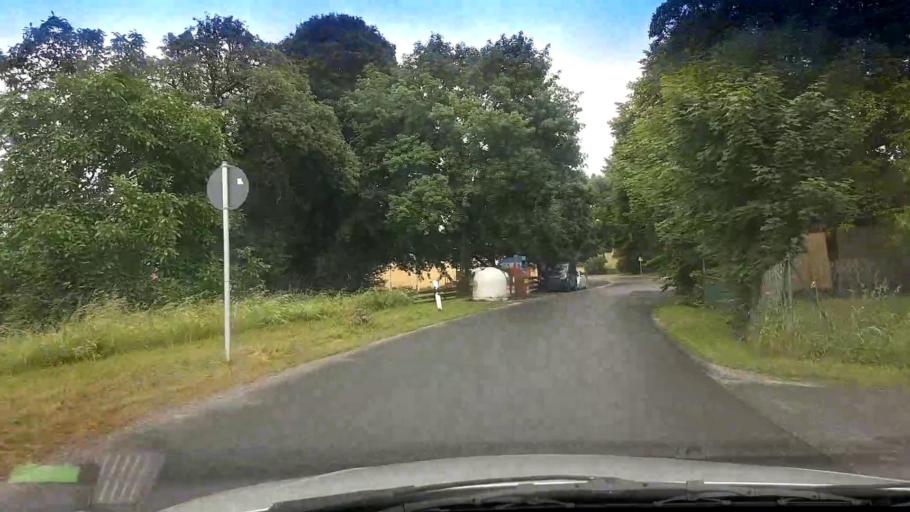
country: DE
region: Bavaria
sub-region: Upper Franconia
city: Wattendorf
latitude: 50.0517
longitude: 11.1381
